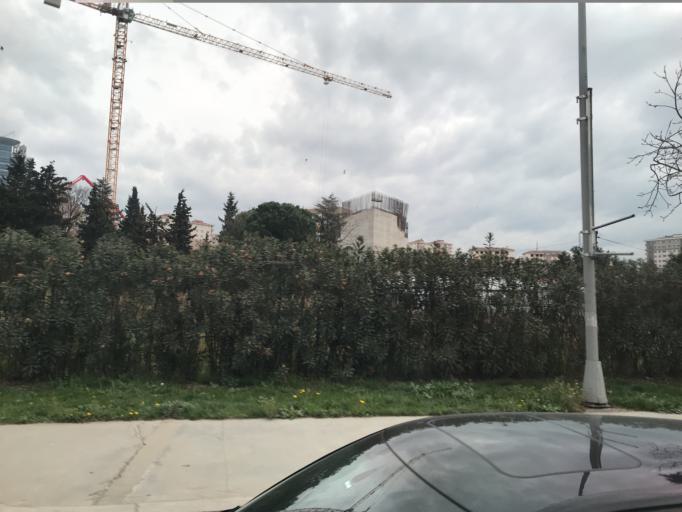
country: TR
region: Istanbul
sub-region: Atasehir
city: Atasehir
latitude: 40.9941
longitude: 29.0698
